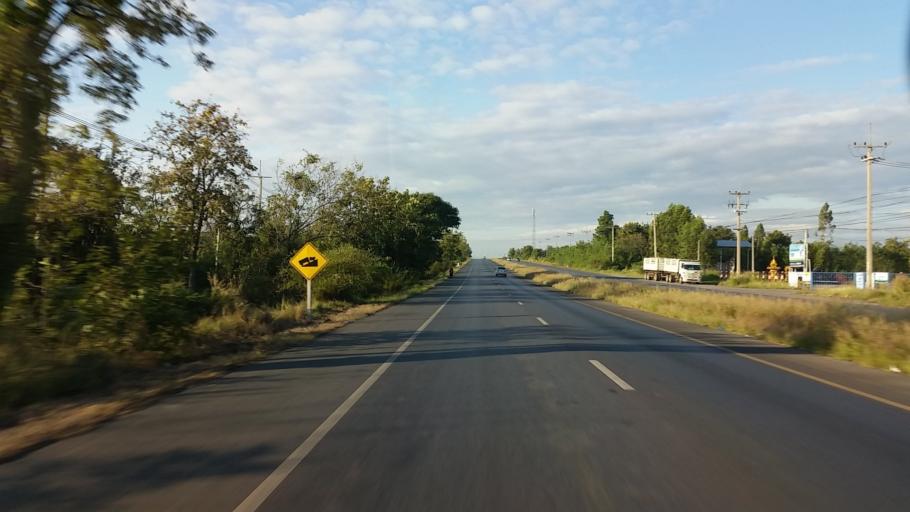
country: TH
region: Lop Buri
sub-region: Amphoe Tha Luang
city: Tha Luang
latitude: 15.0540
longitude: 100.9666
